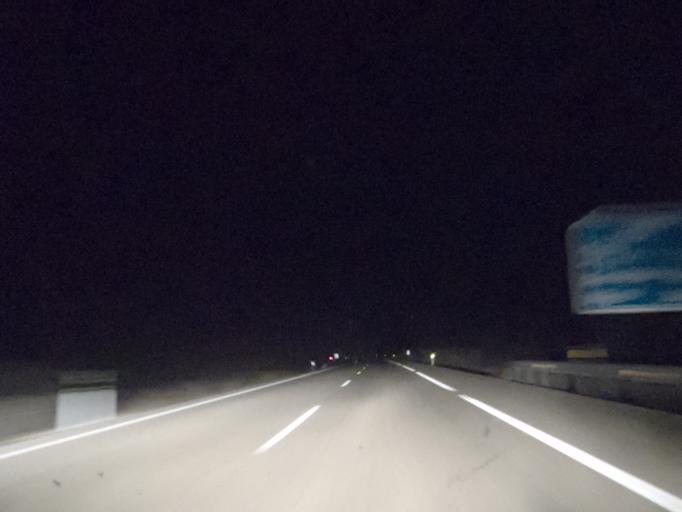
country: ES
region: Castille and Leon
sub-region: Provincia de Zamora
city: Mombuey
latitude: 42.0174
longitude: -6.3155
